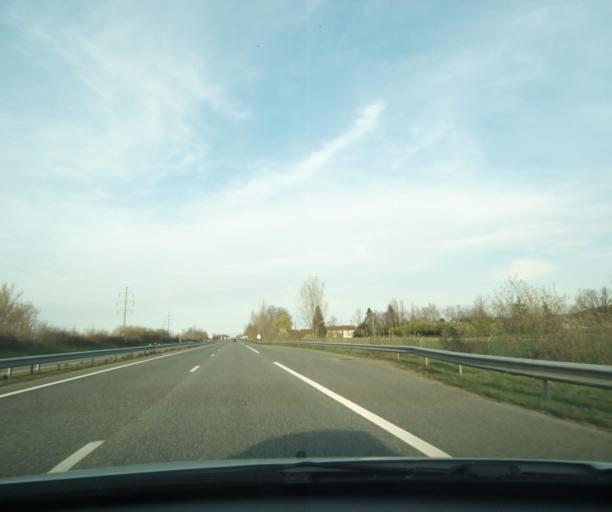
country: FR
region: Midi-Pyrenees
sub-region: Departement de la Haute-Garonne
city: Martres-Tolosane
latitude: 43.1929
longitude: 0.9879
